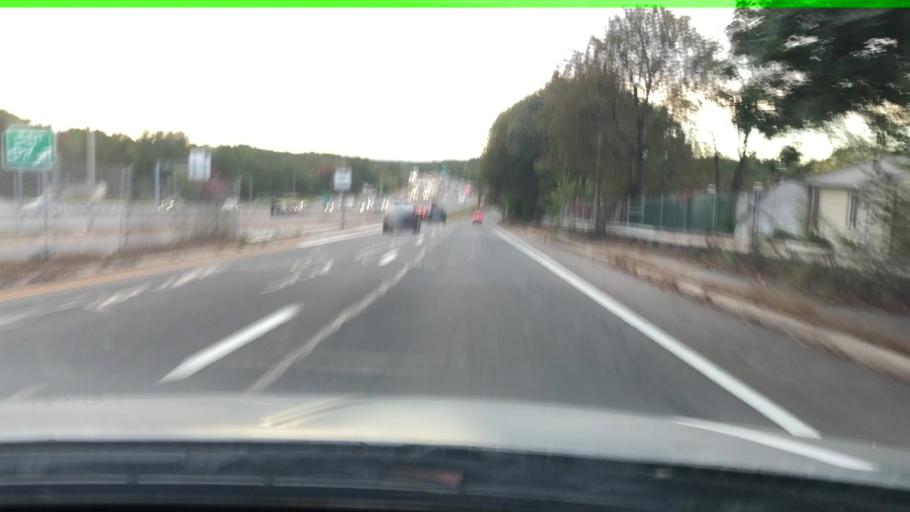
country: US
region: Massachusetts
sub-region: Middlesex County
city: Belmont
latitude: 42.4135
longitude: -71.1887
